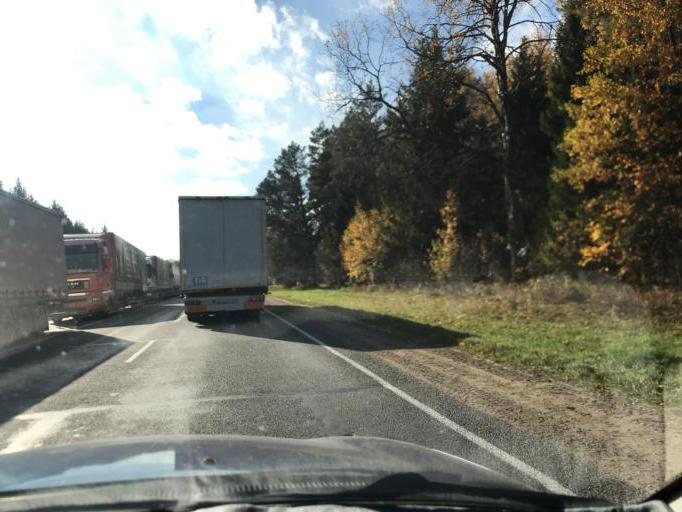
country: LT
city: Salcininkai
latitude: 54.2260
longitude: 25.3571
